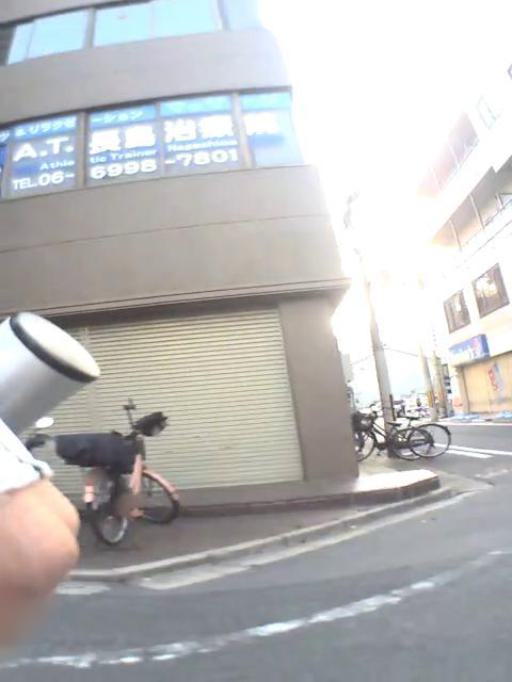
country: JP
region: Osaka
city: Moriguchi
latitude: 34.7364
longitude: 135.5636
